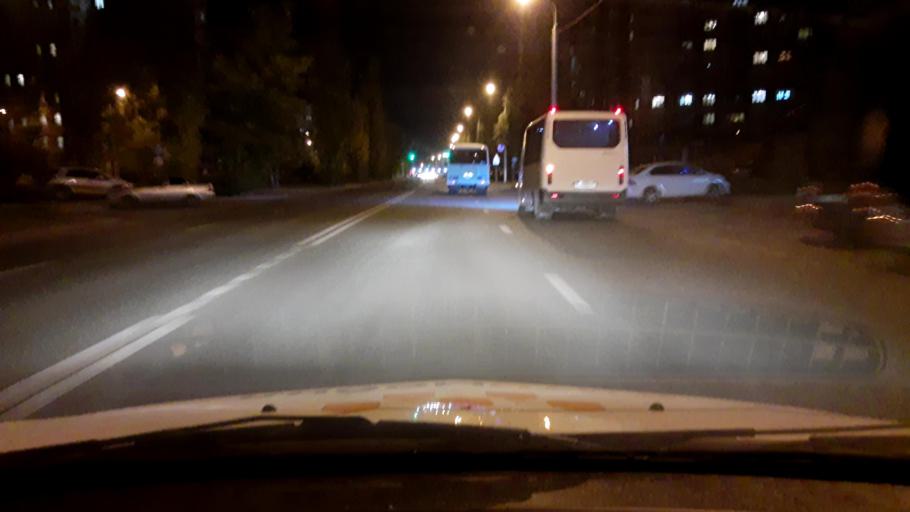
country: RU
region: Bashkortostan
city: Ufa
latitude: 54.7767
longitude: 56.0757
